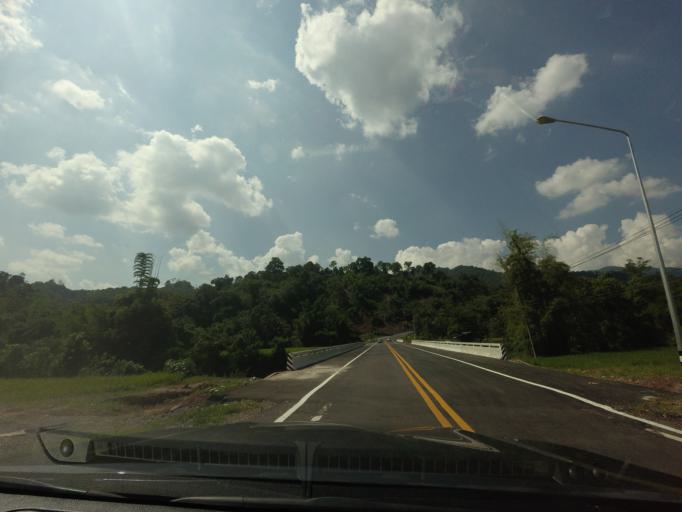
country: TH
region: Nan
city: Bo Kluea
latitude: 19.0797
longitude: 101.1507
